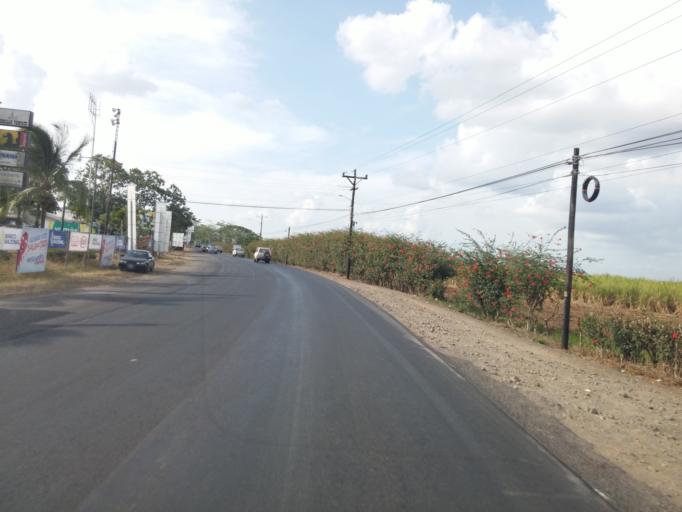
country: CR
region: Alajuela
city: Quesada
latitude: 10.4408
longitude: -84.4656
